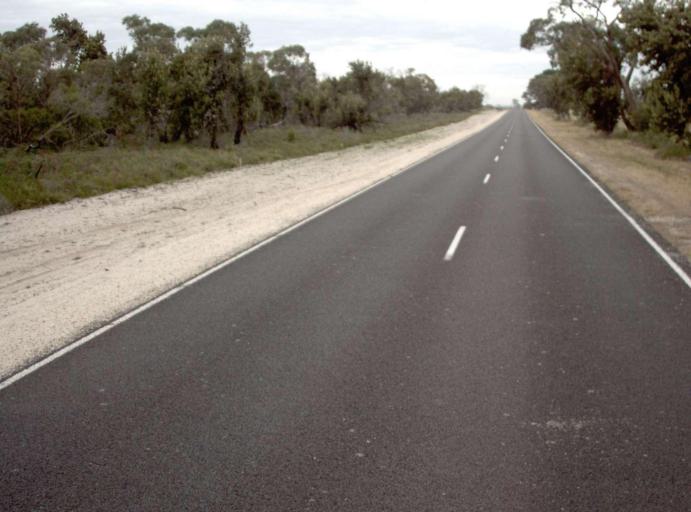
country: AU
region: Victoria
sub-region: Wellington
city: Sale
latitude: -38.1437
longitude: 147.4010
